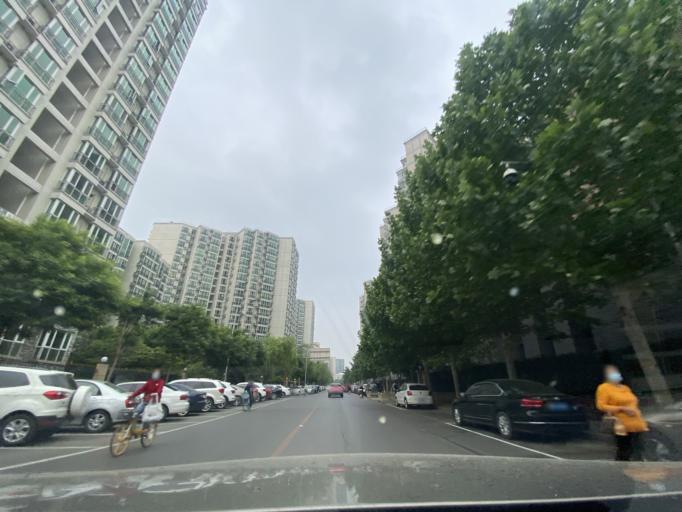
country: CN
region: Beijing
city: Sijiqing
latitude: 39.9581
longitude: 116.2747
